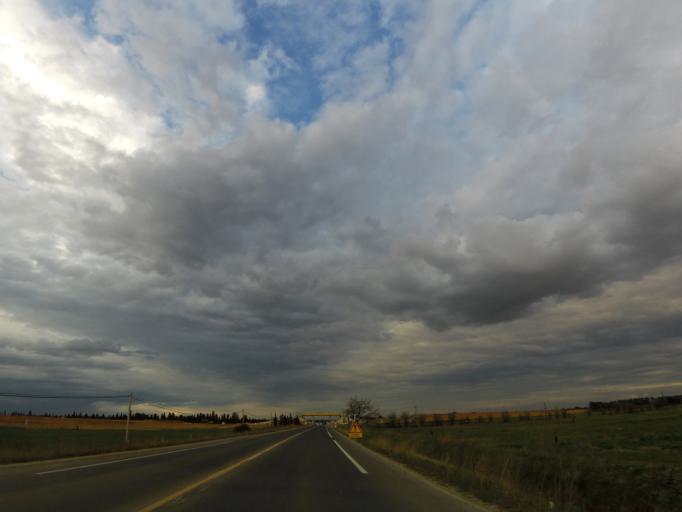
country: FR
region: Languedoc-Roussillon
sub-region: Departement du Gard
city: Vestric-et-Candiac
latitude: 43.7216
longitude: 4.2695
